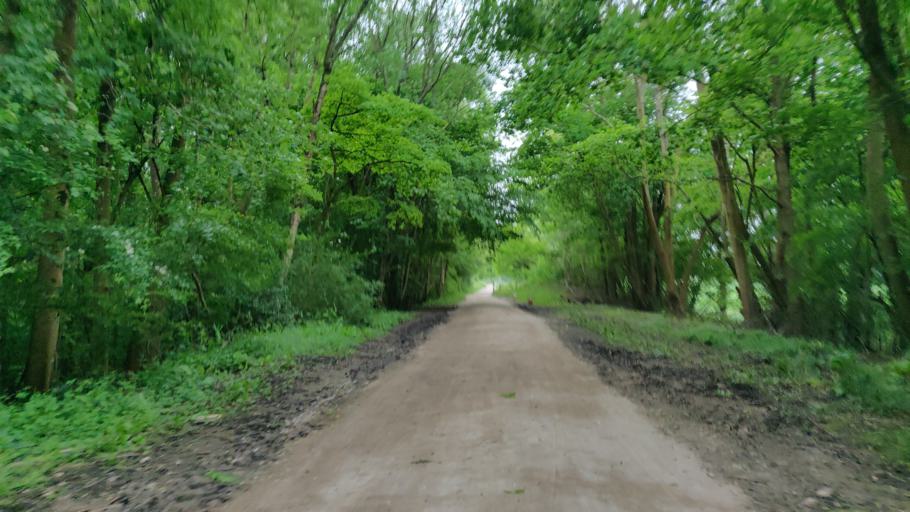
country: GB
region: England
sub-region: West Sussex
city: Partridge Green
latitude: 50.9840
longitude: -0.3149
